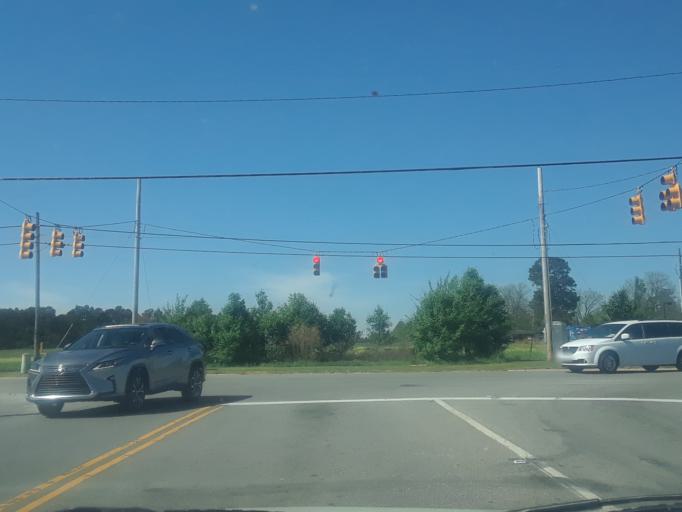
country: US
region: North Carolina
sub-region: Harnett County
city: Dunn
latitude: 35.3135
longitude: -78.6332
